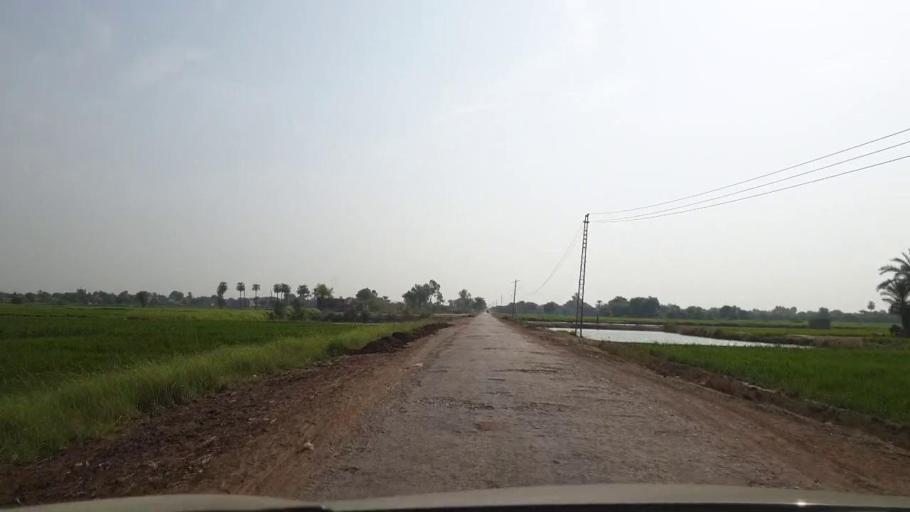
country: PK
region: Sindh
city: Larkana
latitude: 27.4562
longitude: 68.2055
